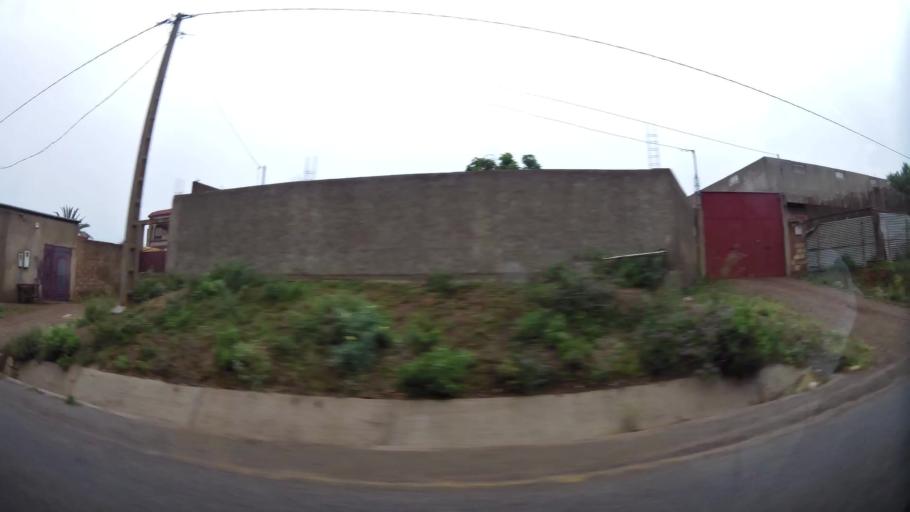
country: MA
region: Oriental
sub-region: Nador
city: Boudinar
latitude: 35.1323
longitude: -3.5915
